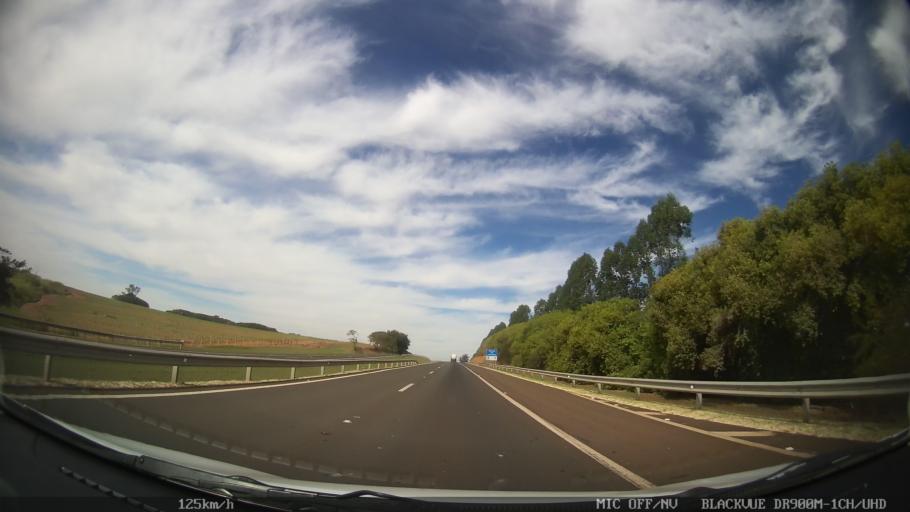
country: BR
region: Sao Paulo
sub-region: Matao
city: Matao
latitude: -21.6034
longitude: -48.4304
